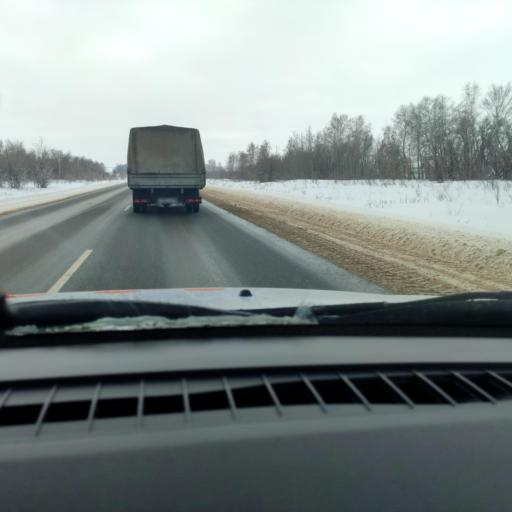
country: RU
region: Samara
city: Dubovyy Umet
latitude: 52.6343
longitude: 50.4895
